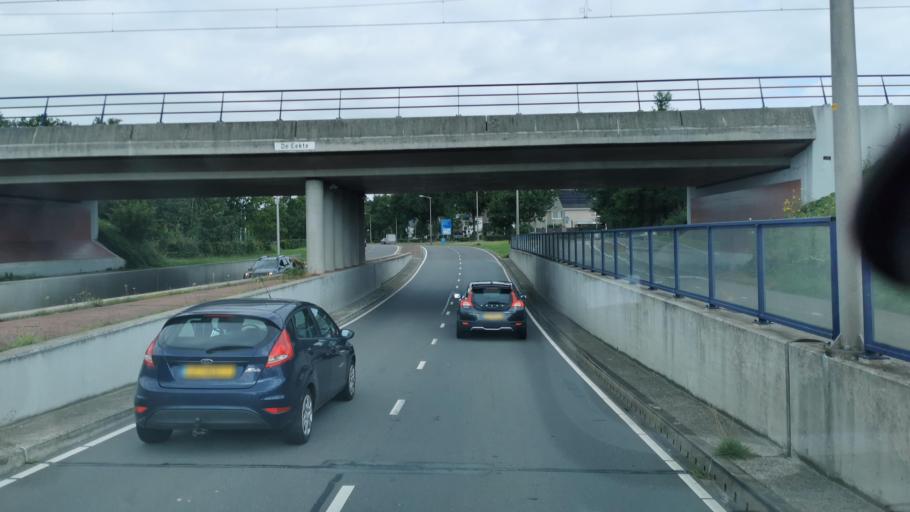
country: NL
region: Overijssel
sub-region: Gemeente Oldenzaal
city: Oldenzaal
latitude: 52.3039
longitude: 6.9219
